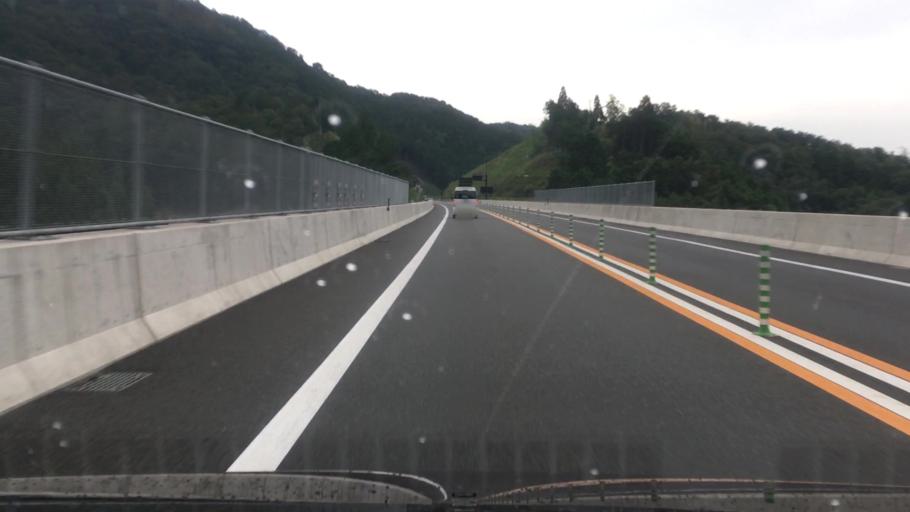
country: JP
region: Hyogo
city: Toyooka
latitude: 35.4377
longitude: 134.7679
